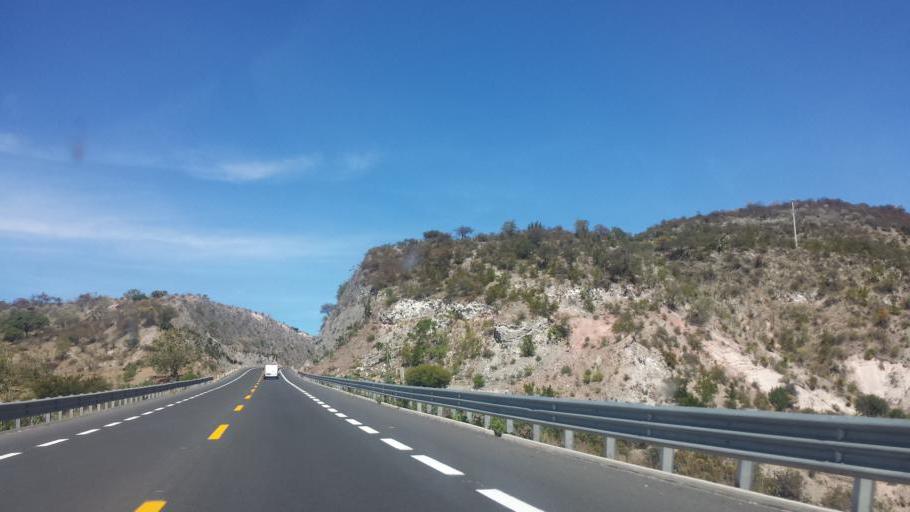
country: MX
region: Oaxaca
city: San Gabriel Casa Blanca
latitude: 17.9731
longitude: -97.3574
